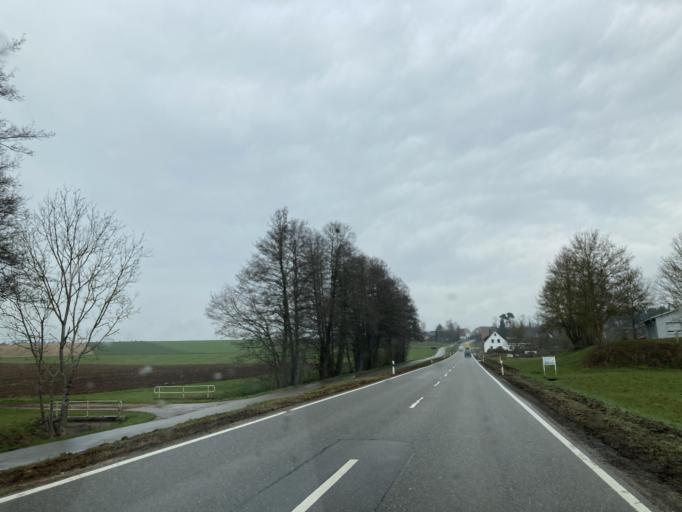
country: DE
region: Baden-Wuerttemberg
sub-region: Freiburg Region
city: Aichhalden
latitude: 48.2502
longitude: 8.4405
